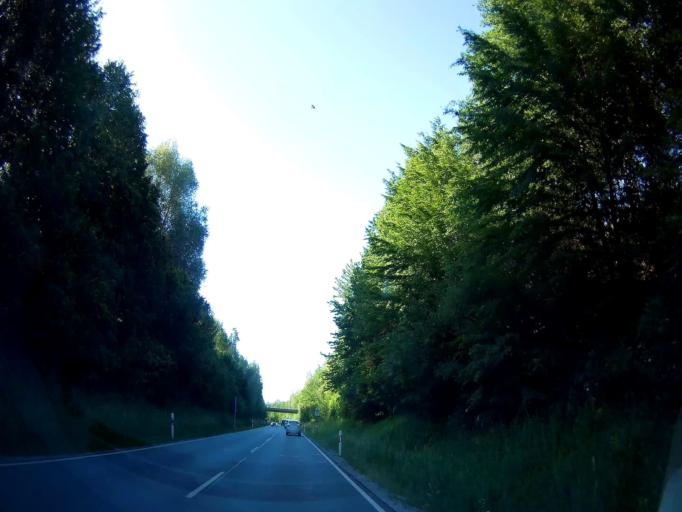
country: DE
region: Bavaria
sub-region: Lower Bavaria
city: Oberschneiding
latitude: 48.7576
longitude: 12.6620
